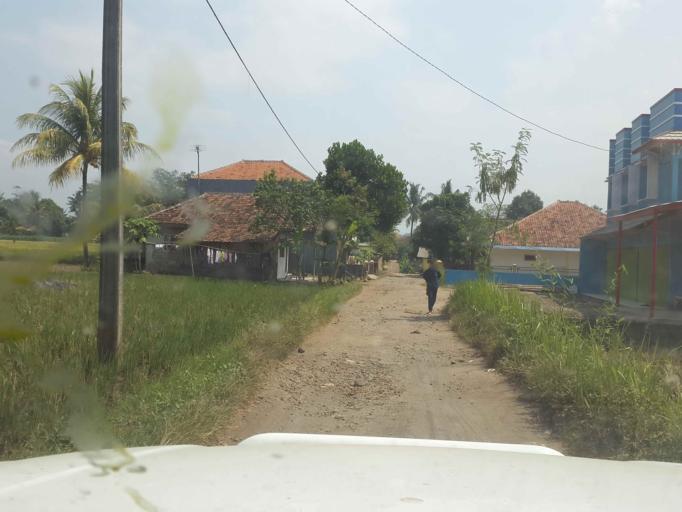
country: ID
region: West Java
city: Ciranjang-hilir
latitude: -6.8810
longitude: 107.2150
